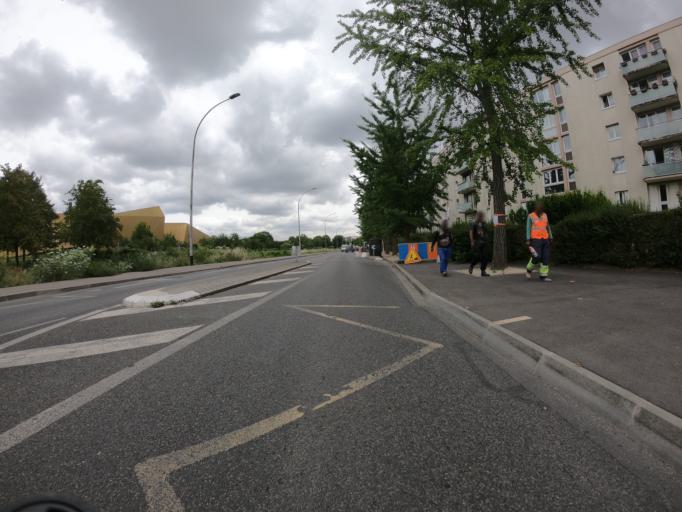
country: FR
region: Ile-de-France
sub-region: Departement des Hauts-de-Seine
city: Bourg-la-Reine
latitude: 48.7674
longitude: 2.3193
